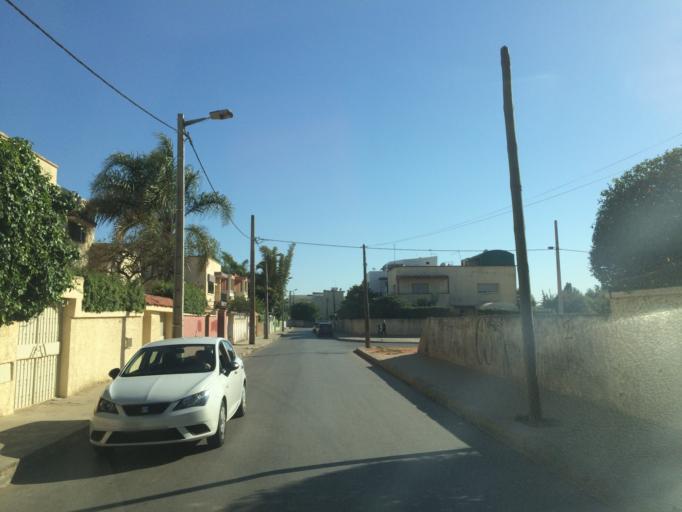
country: MA
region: Rabat-Sale-Zemmour-Zaer
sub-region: Rabat
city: Rabat
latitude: 33.9916
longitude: -6.8213
